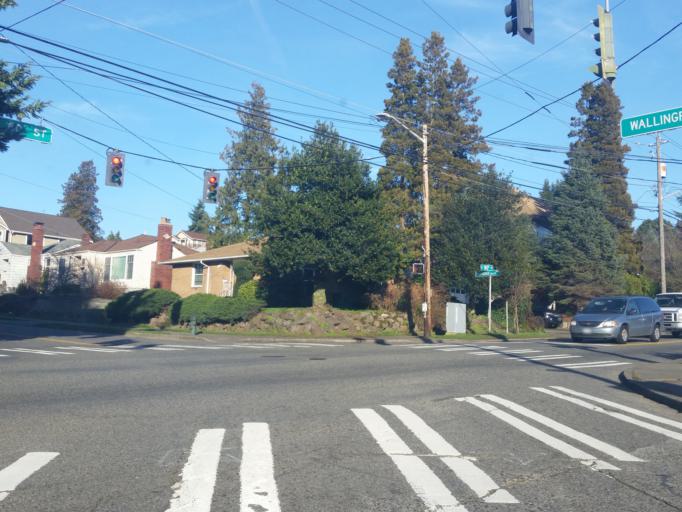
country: US
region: Washington
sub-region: King County
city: Shoreline
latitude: 47.6868
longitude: -122.3366
